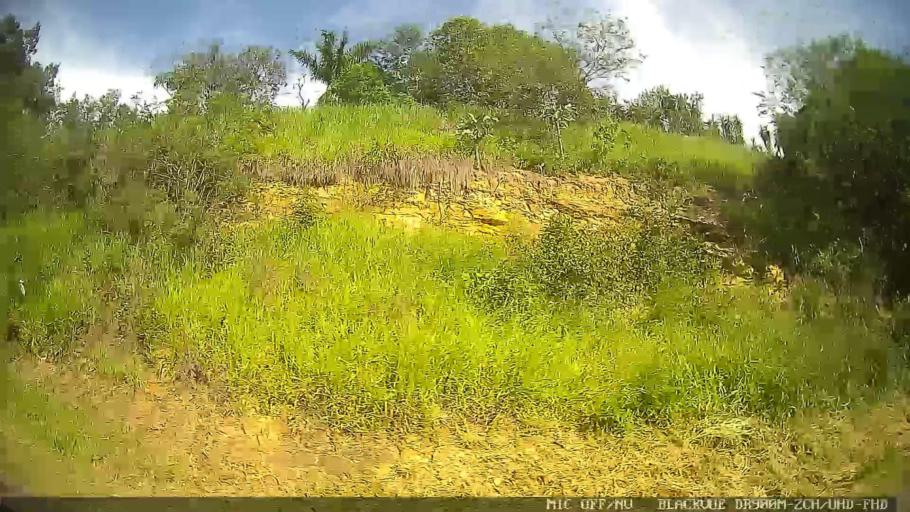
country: BR
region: Sao Paulo
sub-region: Tiete
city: Tiete
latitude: -23.1069
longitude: -47.6943
